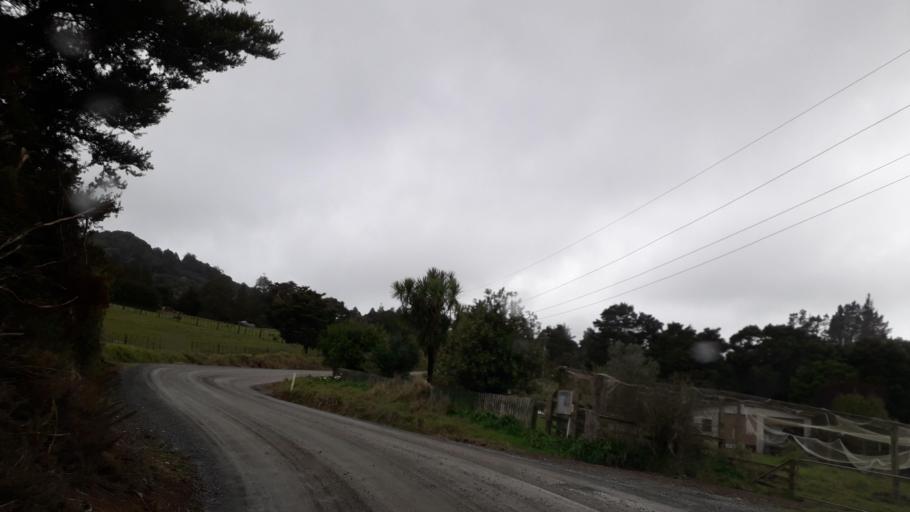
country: NZ
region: Northland
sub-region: Far North District
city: Kerikeri
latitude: -35.1271
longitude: 173.7444
